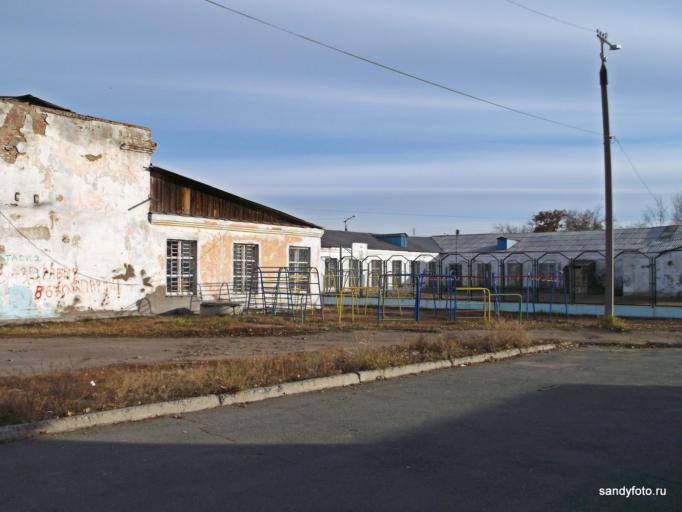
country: RU
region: Chelyabinsk
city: Troitsk
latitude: 54.0966
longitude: 61.5873
